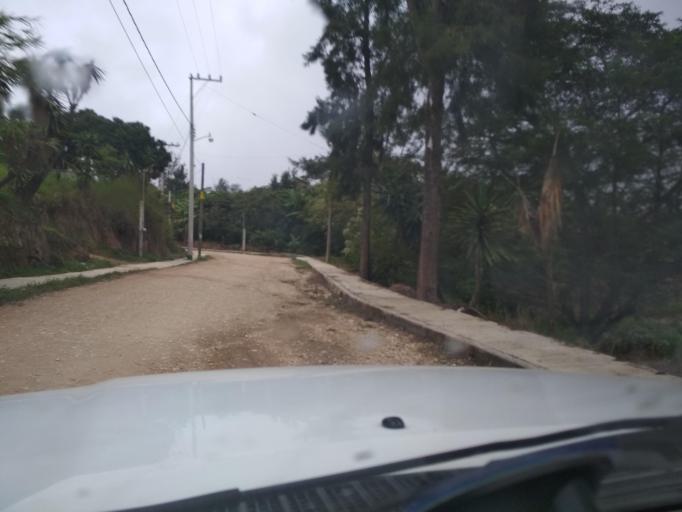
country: MX
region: Veracruz
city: El Castillo
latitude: 19.5426
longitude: -96.8266
